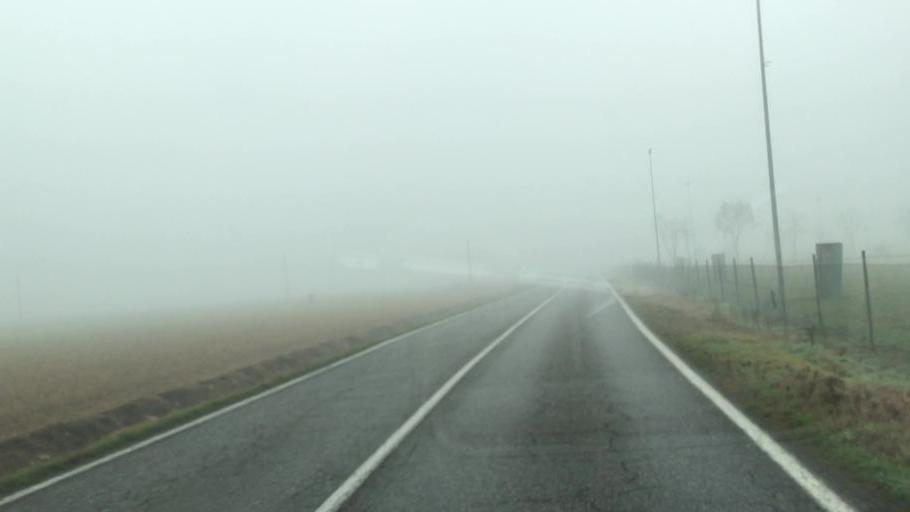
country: IT
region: Lombardy
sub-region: Provincia di Brescia
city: Novagli
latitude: 45.3838
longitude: 10.4095
